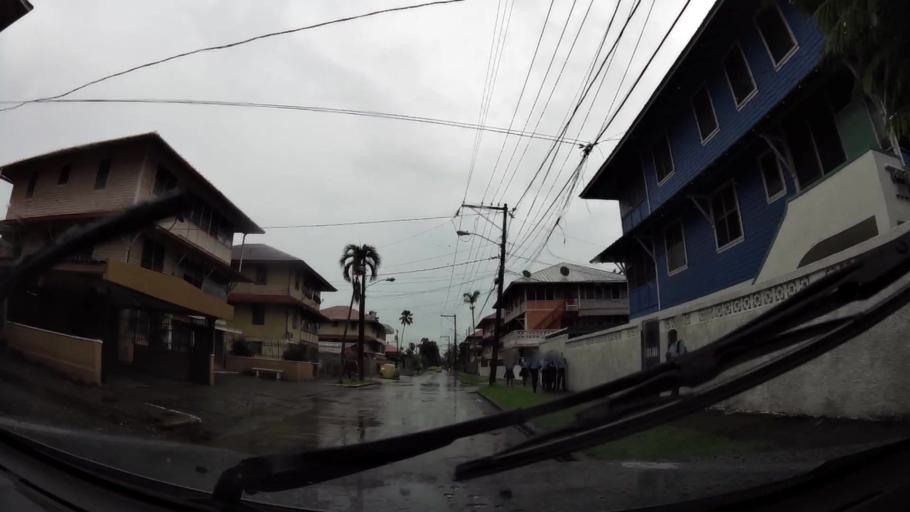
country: PA
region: Colon
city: Colon
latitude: 9.3616
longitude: -79.9002
